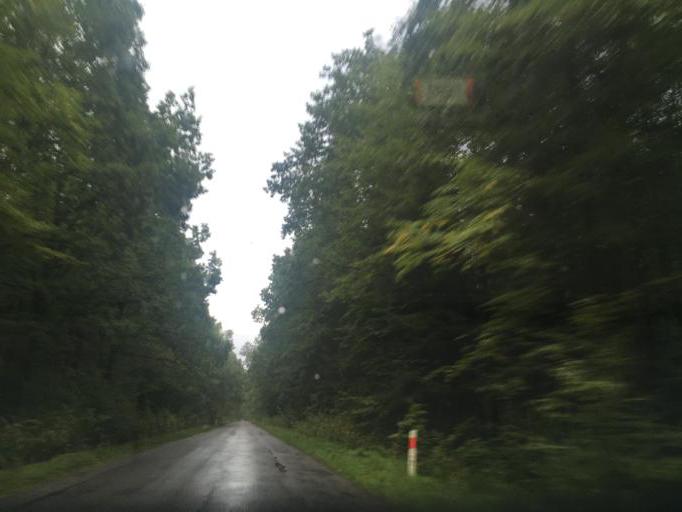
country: PL
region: Podlasie
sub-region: Powiat hajnowski
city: Hajnowka
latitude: 52.8203
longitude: 23.6677
